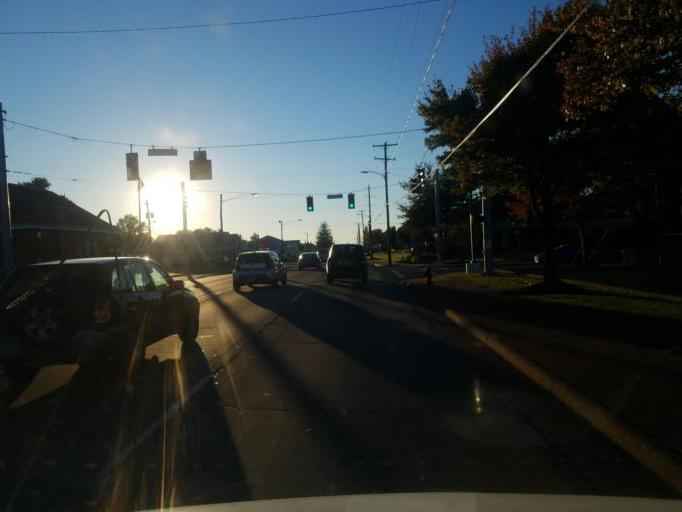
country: US
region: Ohio
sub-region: Stark County
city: Alliance
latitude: 40.9019
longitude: -81.1236
